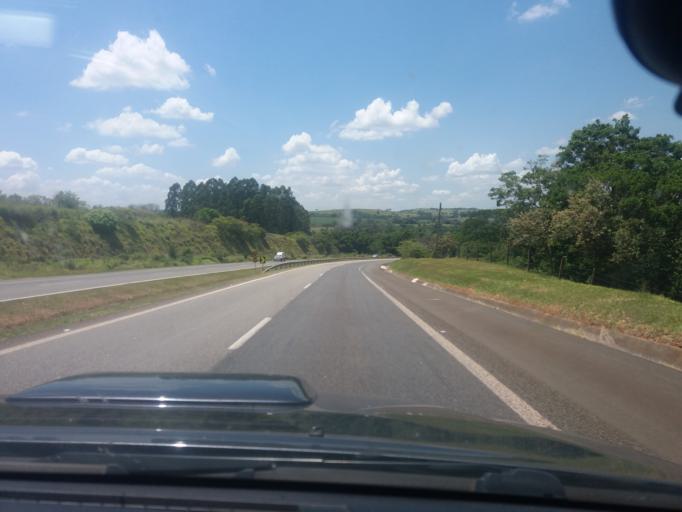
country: BR
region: Sao Paulo
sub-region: Tatui
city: Tatui
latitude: -23.4042
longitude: -47.9237
